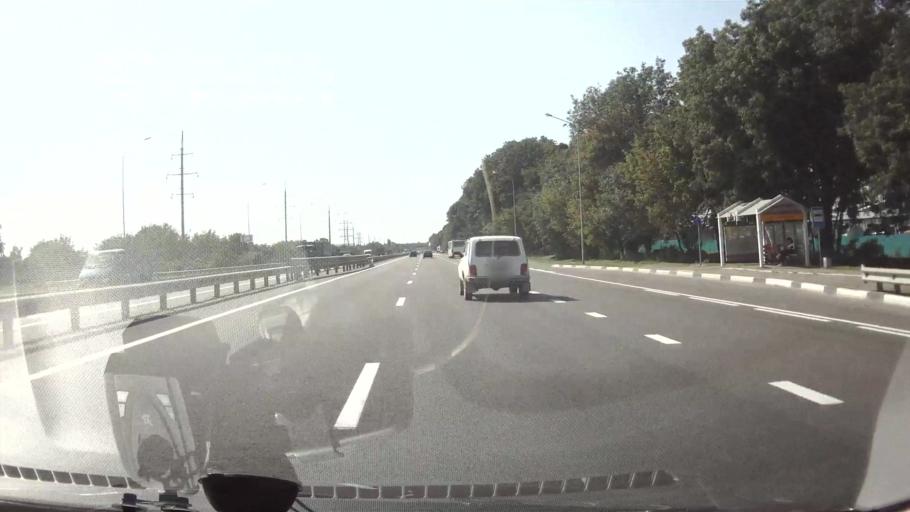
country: RU
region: Krasnodarskiy
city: Starokorsunskaya
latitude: 45.0258
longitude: 39.2162
